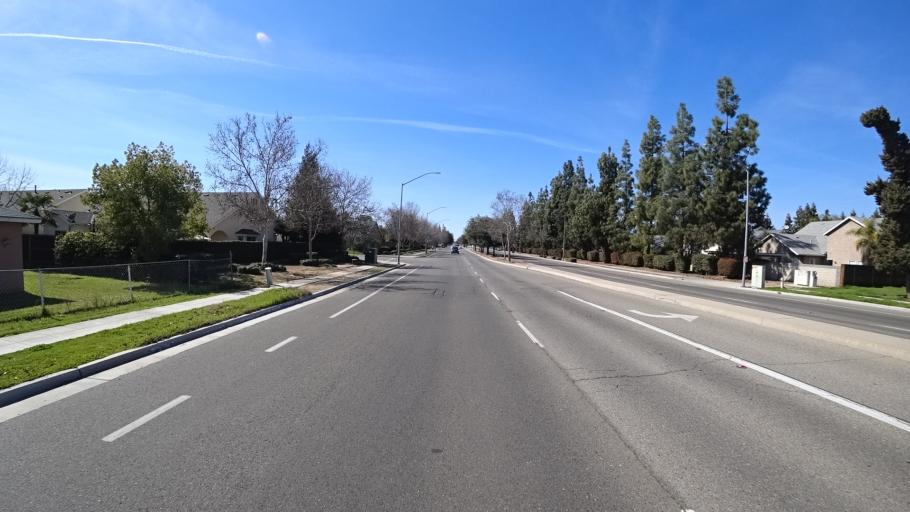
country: US
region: California
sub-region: Fresno County
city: Clovis
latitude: 36.8520
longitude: -119.7436
